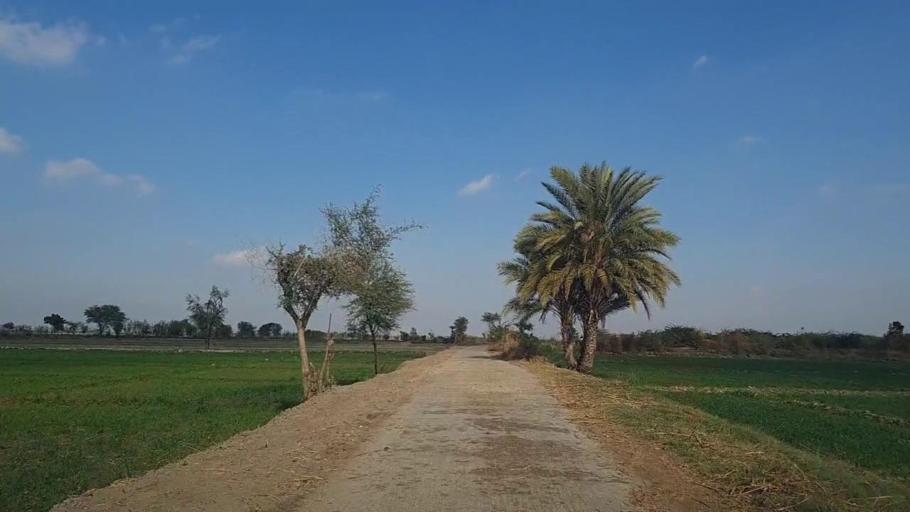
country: PK
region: Sindh
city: Tando Mittha Khan
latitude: 25.9941
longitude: 69.2477
